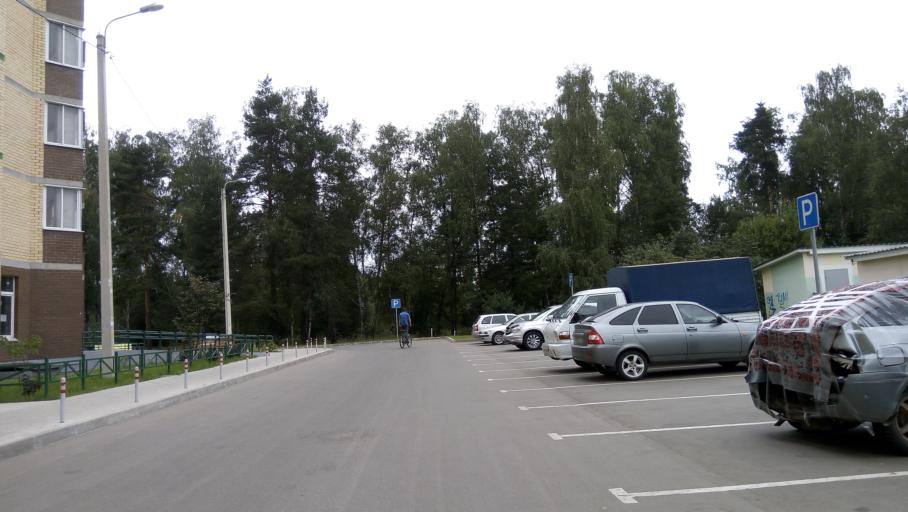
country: RU
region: Moskovskaya
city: Zelenogradskiy
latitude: 56.0912
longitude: 37.8999
